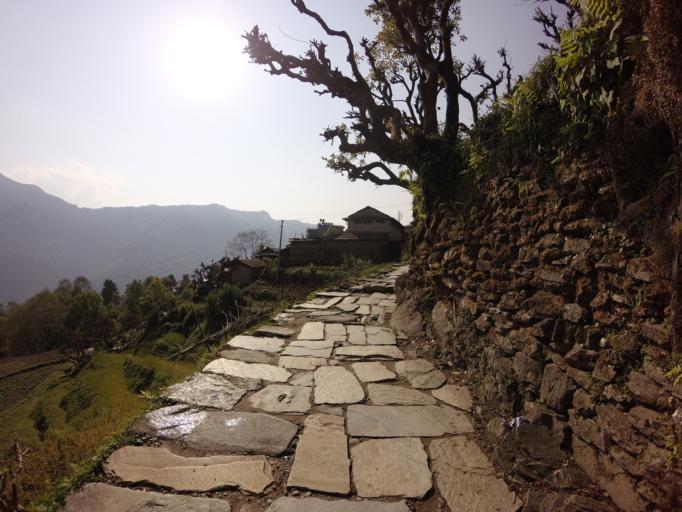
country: NP
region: Western Region
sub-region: Dhawalagiri Zone
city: Chitre
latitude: 28.3787
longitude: 83.8071
